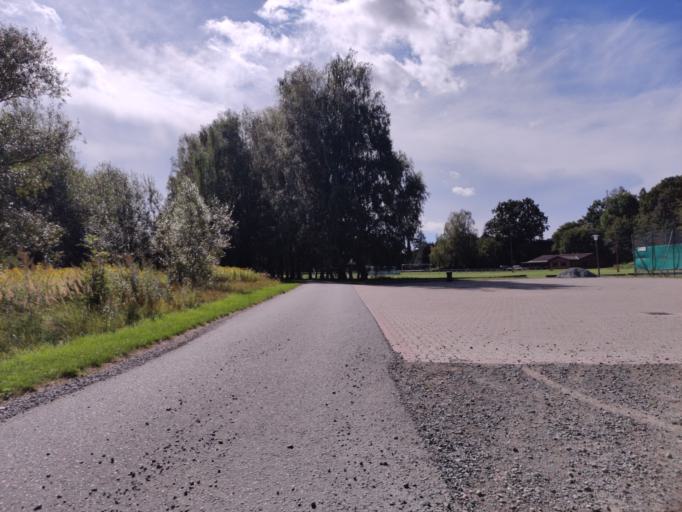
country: DE
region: Lower Saxony
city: Baddeckenstedt
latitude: 52.0813
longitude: 10.2352
